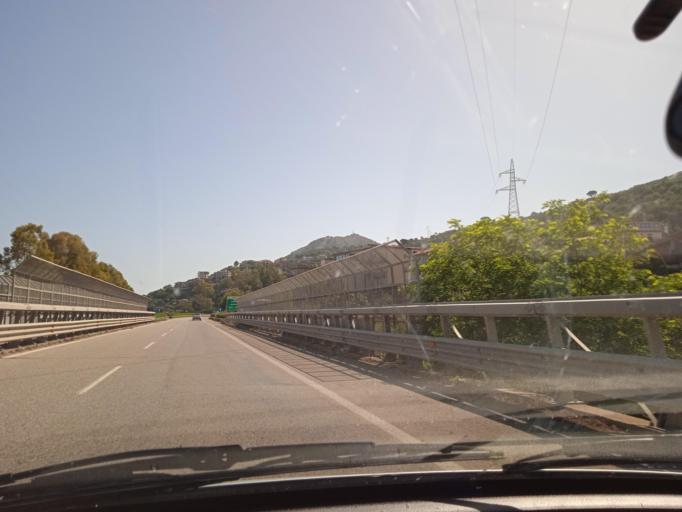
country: IT
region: Sicily
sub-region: Messina
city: Brolo
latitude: 38.1500
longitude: 14.8310
